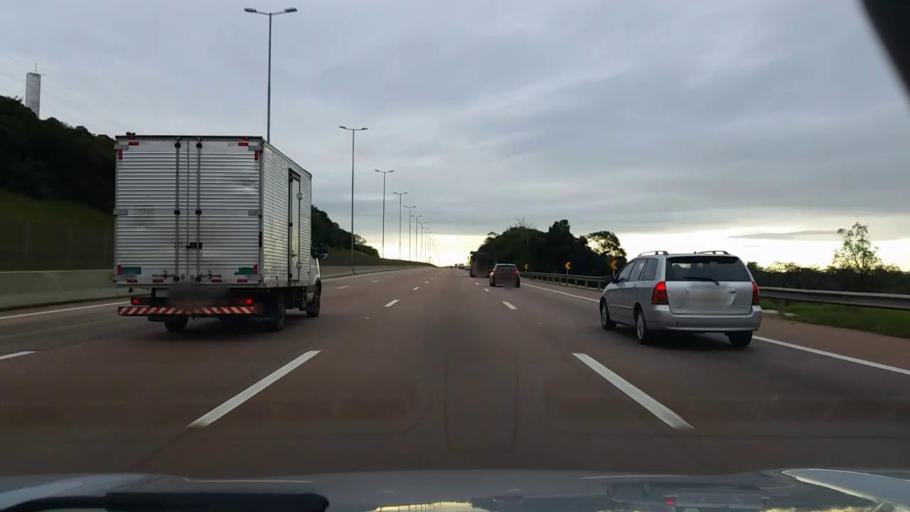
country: BR
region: Rio Grande do Sul
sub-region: Gravatai
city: Gravatai
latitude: -29.9563
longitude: -51.0113
